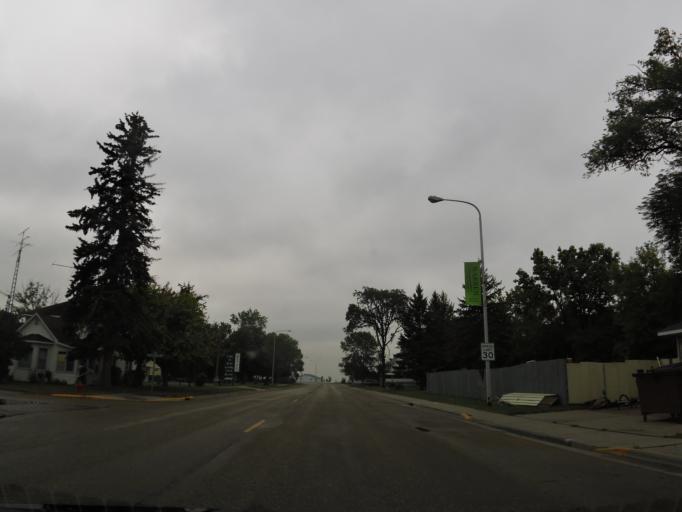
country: US
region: Minnesota
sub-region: Marshall County
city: Warren
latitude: 48.2006
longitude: -96.7715
